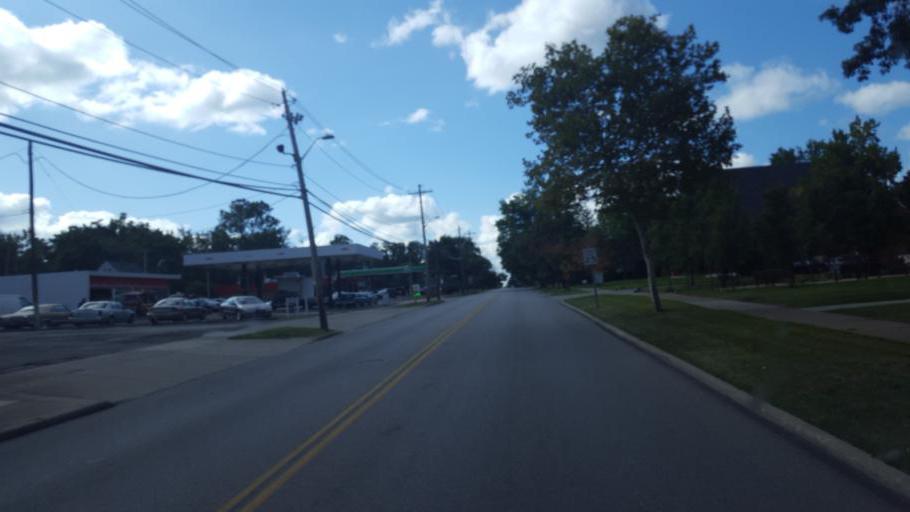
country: US
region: Ohio
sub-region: Lorain County
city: Oberlin
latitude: 41.2883
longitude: -82.2176
